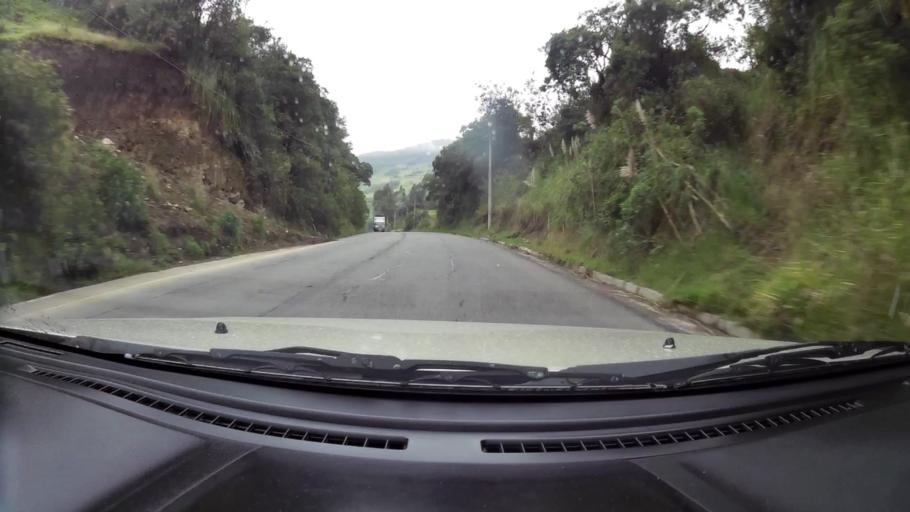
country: EC
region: Canar
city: Canar
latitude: -2.4017
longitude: -78.9747
